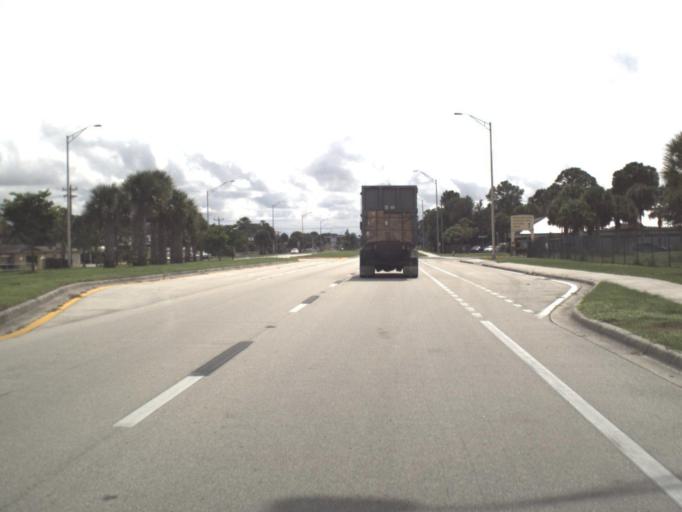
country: US
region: Florida
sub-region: Lee County
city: Palmona Park
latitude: 26.6896
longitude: -81.8868
